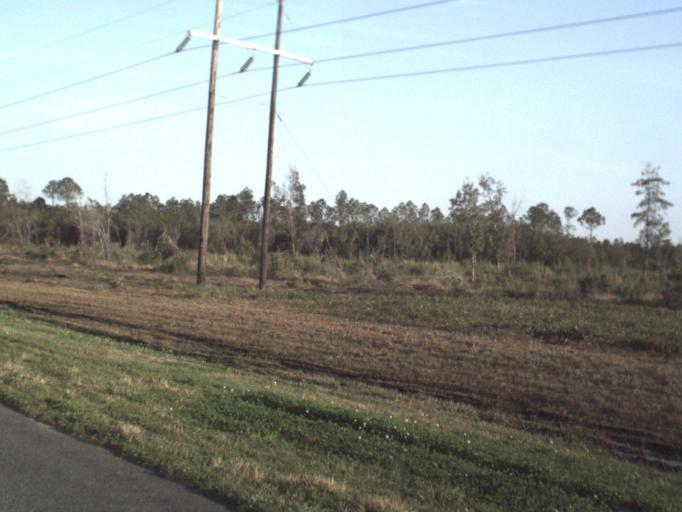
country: US
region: Florida
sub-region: Bay County
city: Laguna Beach
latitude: 30.4400
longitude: -85.8128
